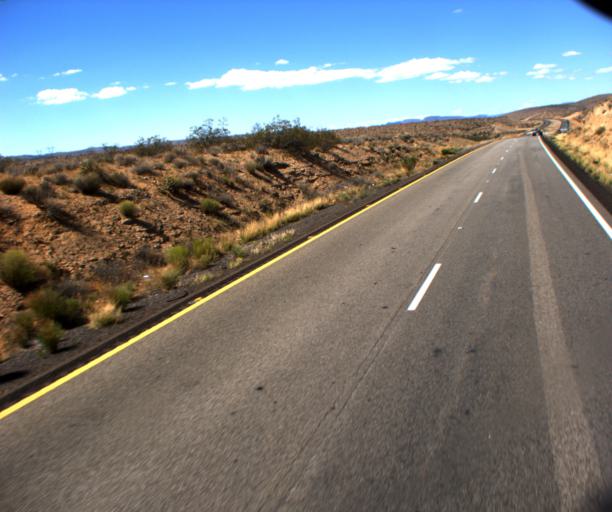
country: US
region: Arizona
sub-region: Mohave County
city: Kingman
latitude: 34.9833
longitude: -113.6675
